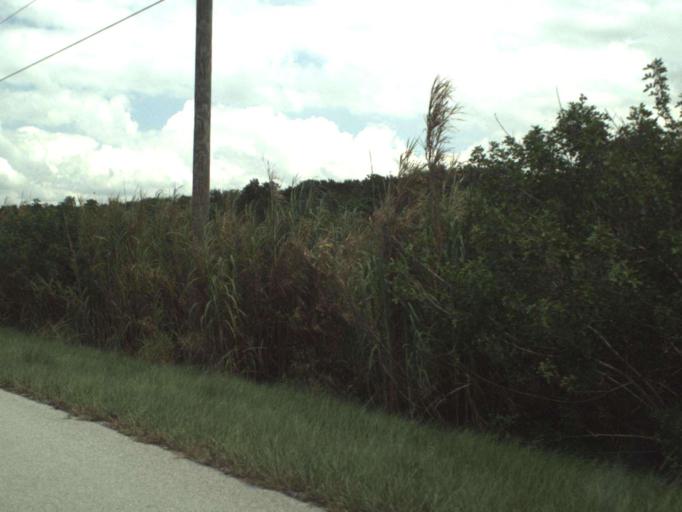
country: US
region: Florida
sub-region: Okeechobee County
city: Taylor Creek
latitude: 27.1193
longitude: -80.6732
